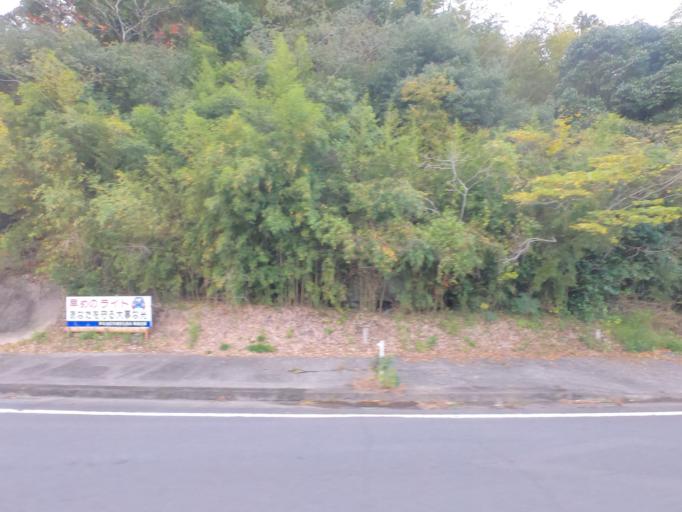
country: JP
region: Kumamoto
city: Minamata
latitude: 32.2574
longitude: 130.5099
